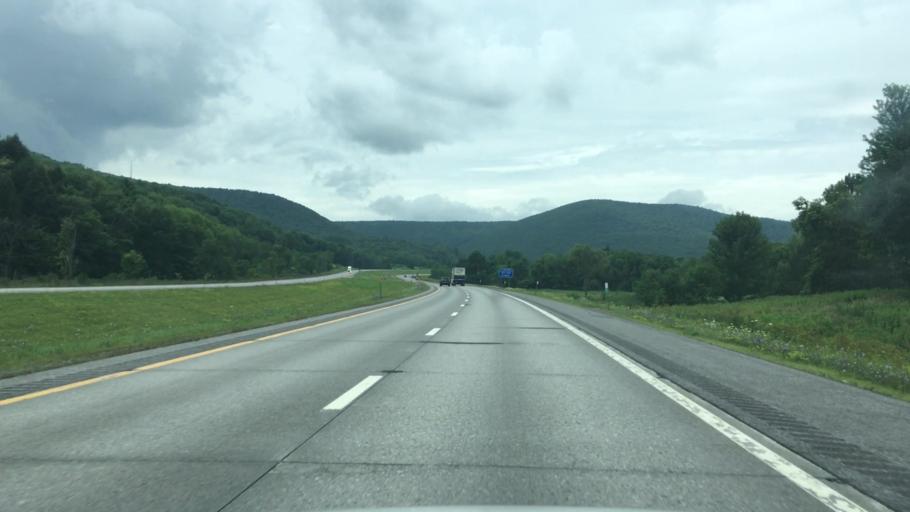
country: US
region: New York
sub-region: Schoharie County
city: Cobleskill
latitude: 42.6492
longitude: -74.6049
